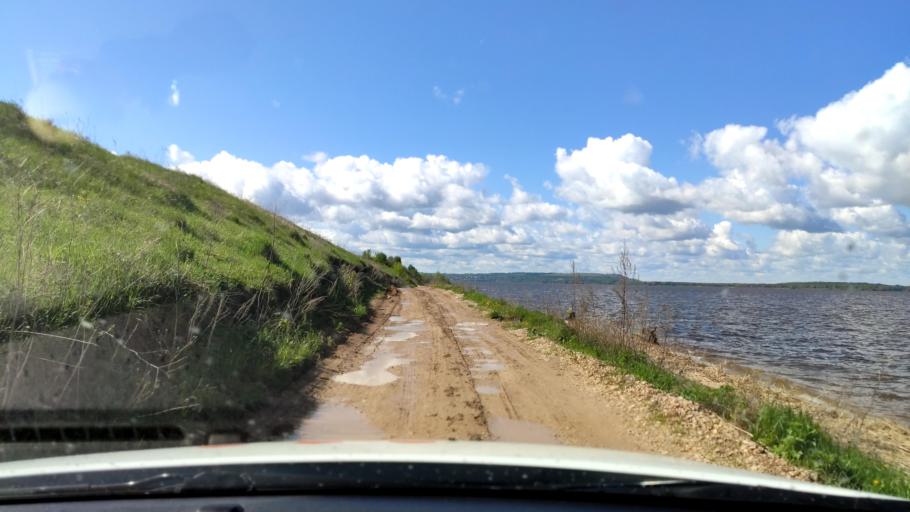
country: RU
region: Tatarstan
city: Sviyazhsk
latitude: 55.7733
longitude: 48.6885
